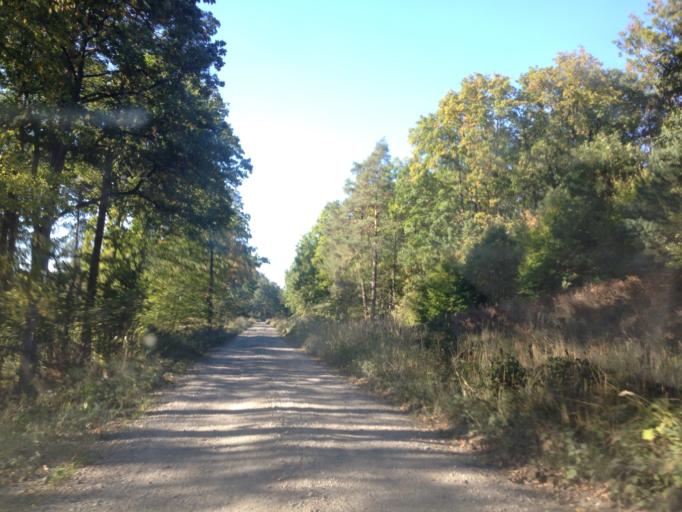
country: PL
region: Kujawsko-Pomorskie
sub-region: Powiat brodnicki
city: Gorzno
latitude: 53.2386
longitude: 19.6883
